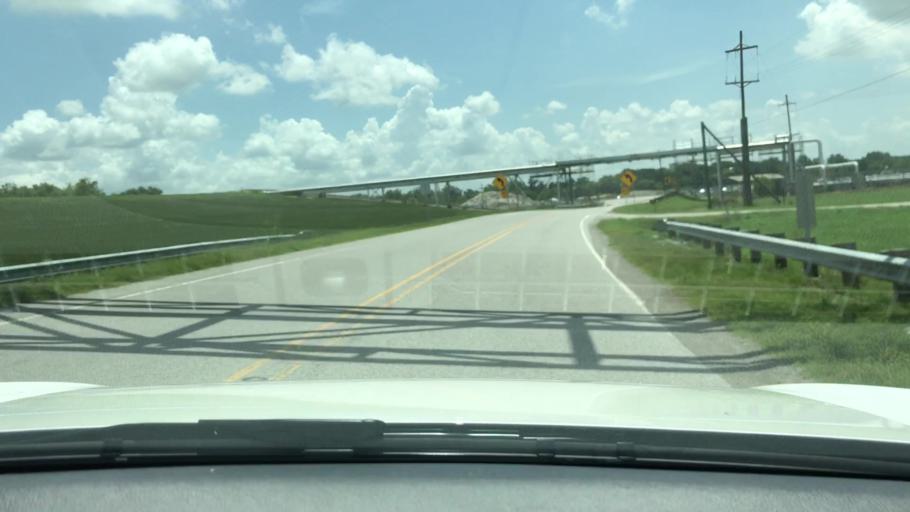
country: US
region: Louisiana
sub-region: Iberville Parish
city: Plaquemine
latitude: 30.2734
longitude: -91.1723
